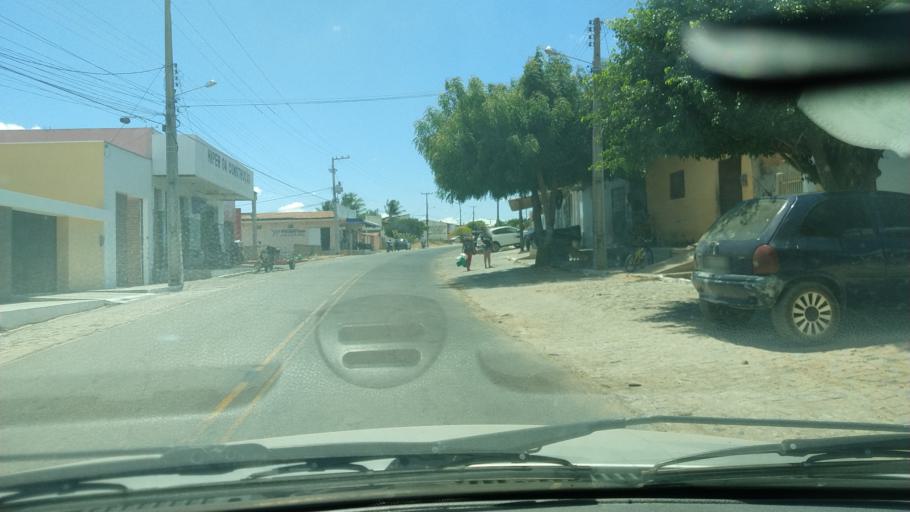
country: BR
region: Rio Grande do Norte
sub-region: Cerro Cora
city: Cerro Cora
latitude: -6.0521
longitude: -36.3541
